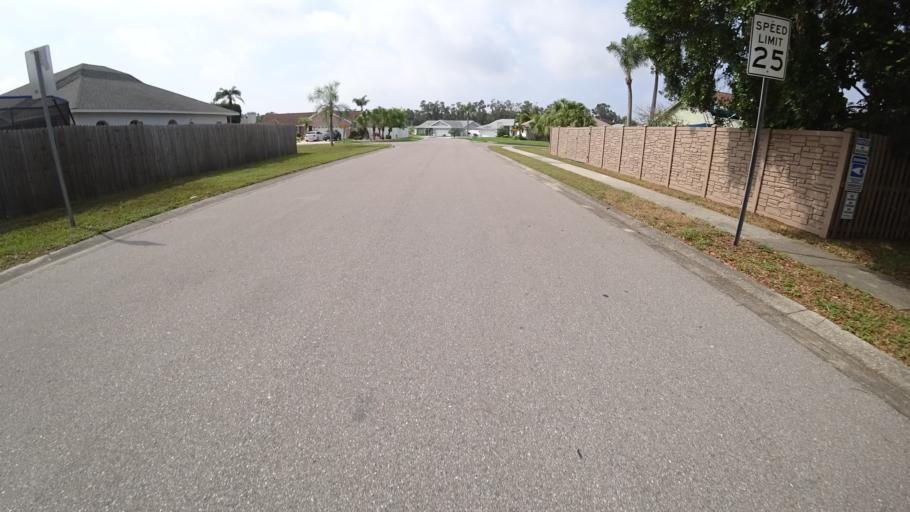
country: US
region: Florida
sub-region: Manatee County
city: West Bradenton
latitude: 27.4832
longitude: -82.6153
